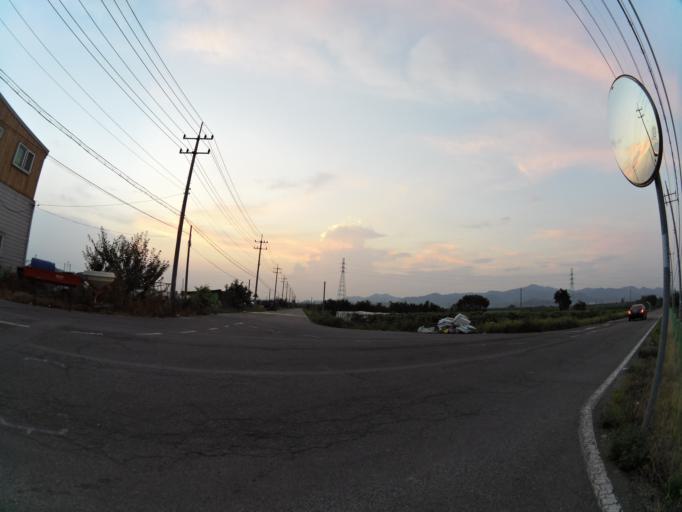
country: KR
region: Gyeongsangbuk-do
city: Gyeongsan-si
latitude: 35.8475
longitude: 128.7456
